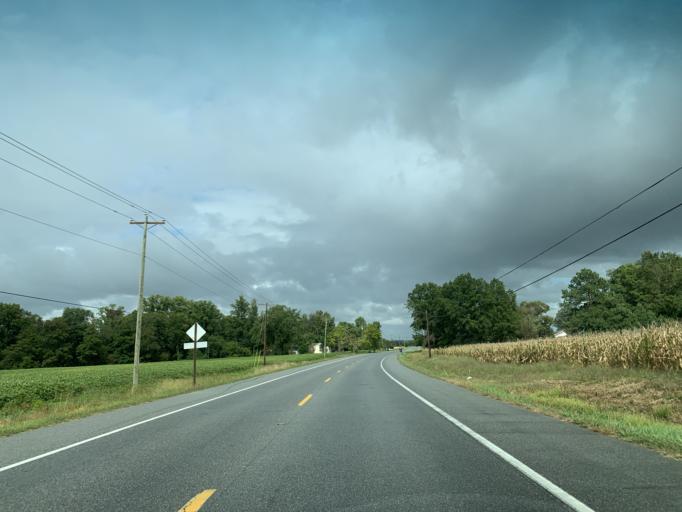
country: US
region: Maryland
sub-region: Caroline County
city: Ridgely
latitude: 38.9640
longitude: -75.8861
